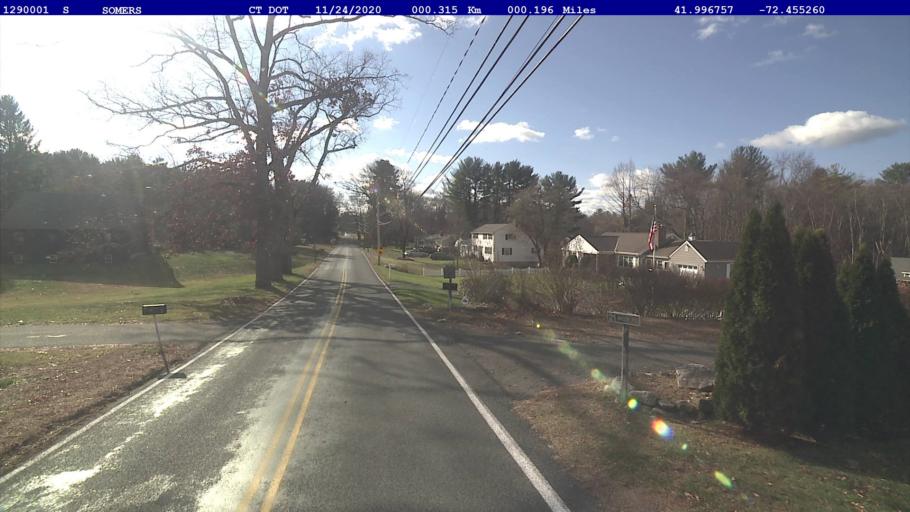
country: US
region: Connecticut
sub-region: Tolland County
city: Somers
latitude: 41.9968
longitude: -72.4553
